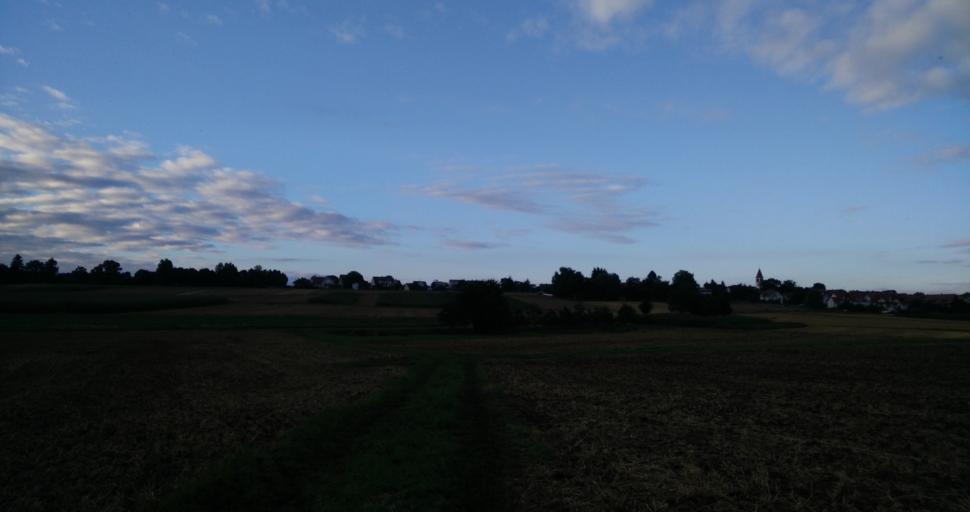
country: DE
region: Baden-Wuerttemberg
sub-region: Tuebingen Region
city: Gomaringen
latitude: 48.4674
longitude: 9.0803
